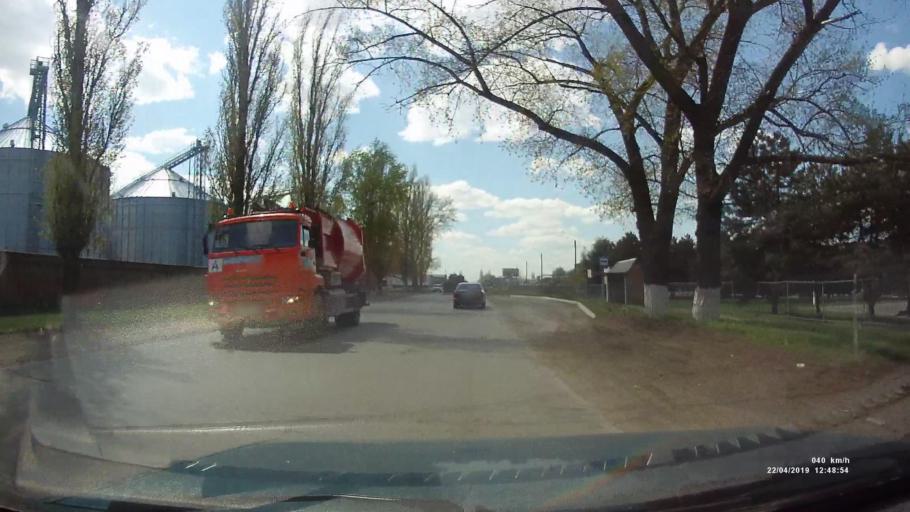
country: RU
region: Rostov
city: Azov
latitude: 47.0941
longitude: 39.4006
